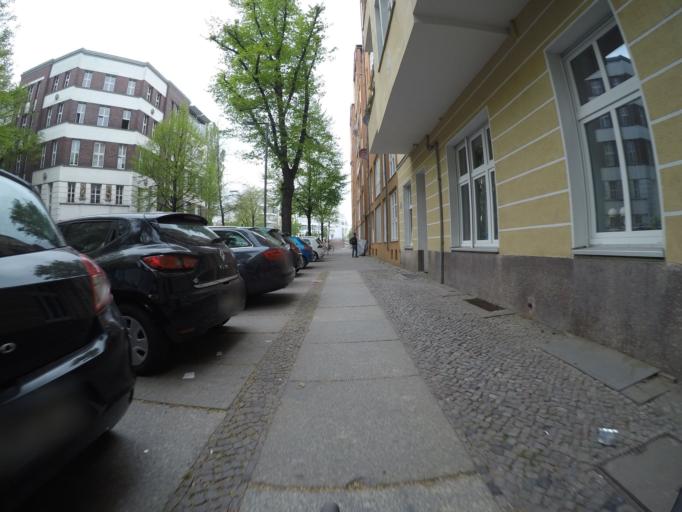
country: DE
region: Berlin
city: Moabit
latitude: 52.5224
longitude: 13.3247
